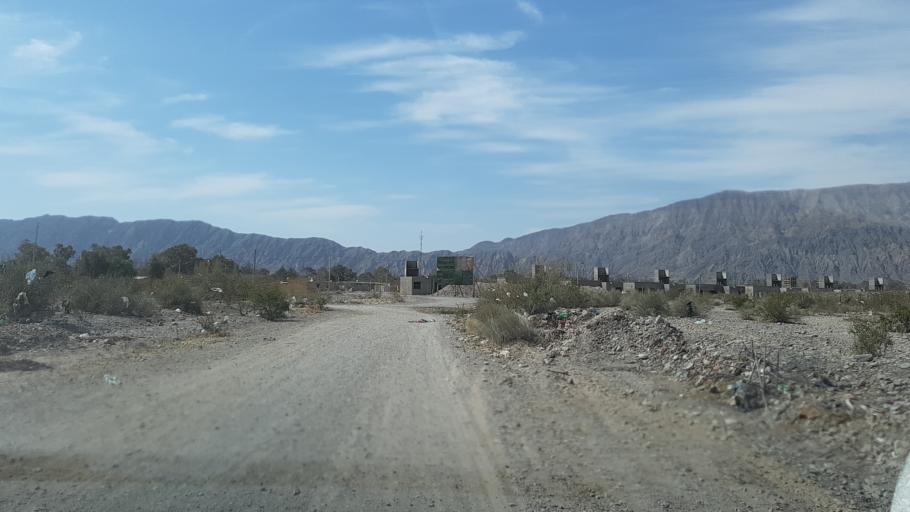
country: AR
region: San Juan
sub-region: Departamento de Zonda
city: Zonda
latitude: -31.5474
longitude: -68.7403
